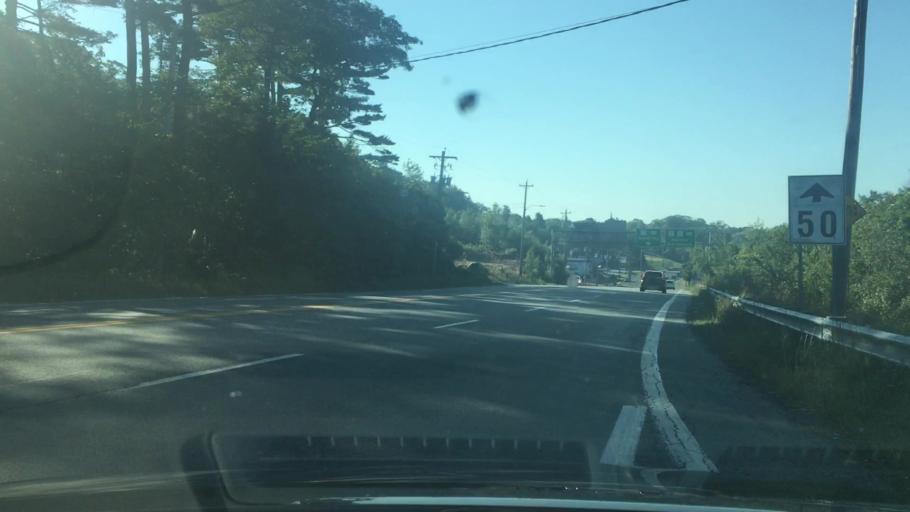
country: CA
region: Nova Scotia
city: Dartmouth
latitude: 44.7426
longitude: -63.6557
